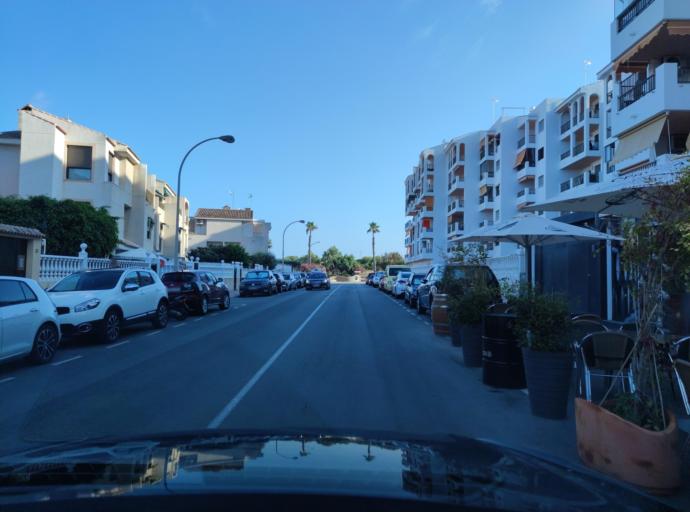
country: ES
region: Valencia
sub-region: Provincia de Alicante
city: Guardamar del Segura
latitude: 38.0810
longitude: -0.6516
